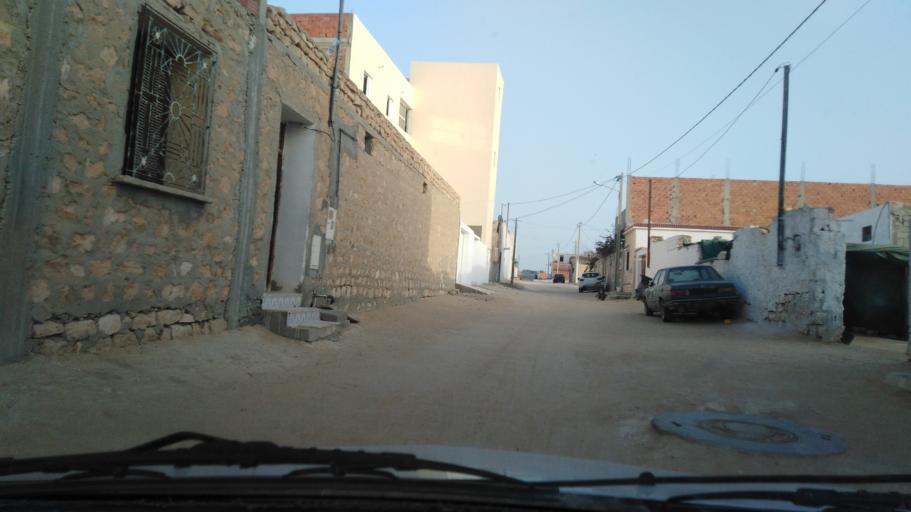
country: TN
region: Qabis
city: Gabes
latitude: 33.9533
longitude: 9.9954
